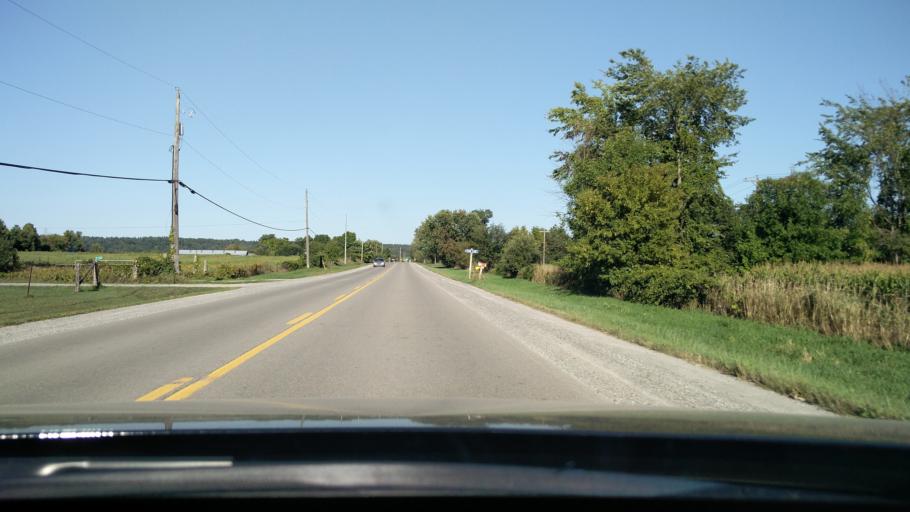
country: CA
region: Ontario
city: Perth
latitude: 44.6704
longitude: -76.4266
